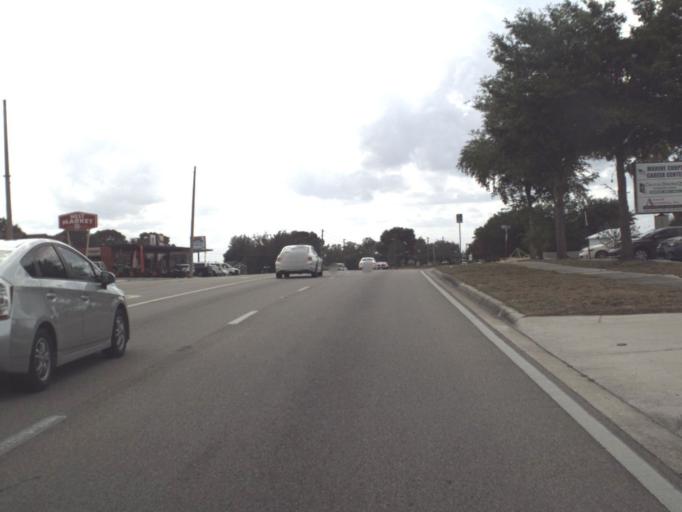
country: US
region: Florida
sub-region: Lake County
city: Clermont
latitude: 28.5517
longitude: -81.7714
